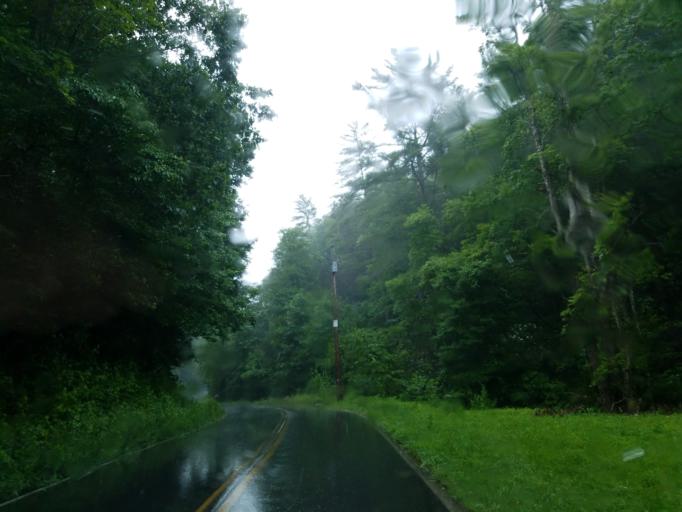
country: US
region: Georgia
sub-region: Fannin County
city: Blue Ridge
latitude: 34.7825
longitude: -84.2837
